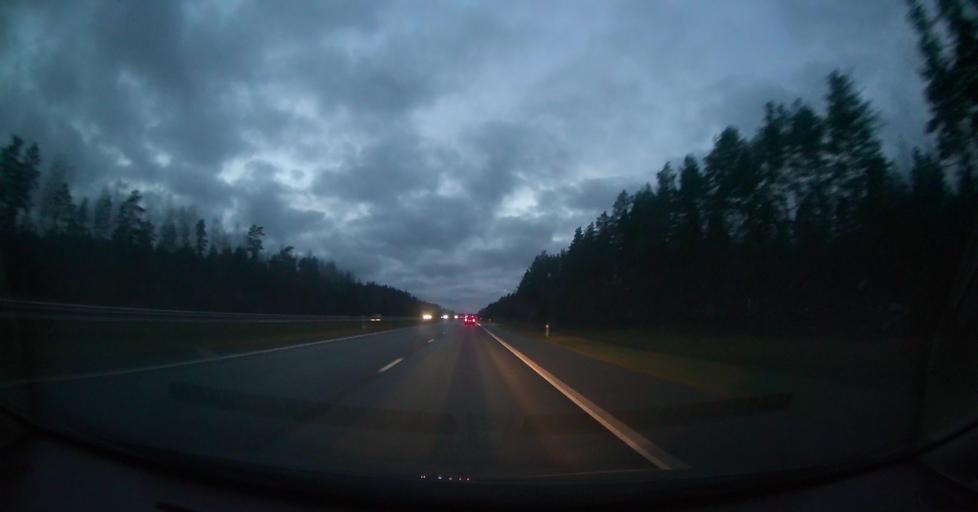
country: EE
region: Harju
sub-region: Kuusalu vald
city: Kuusalu
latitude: 59.4536
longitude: 25.4928
